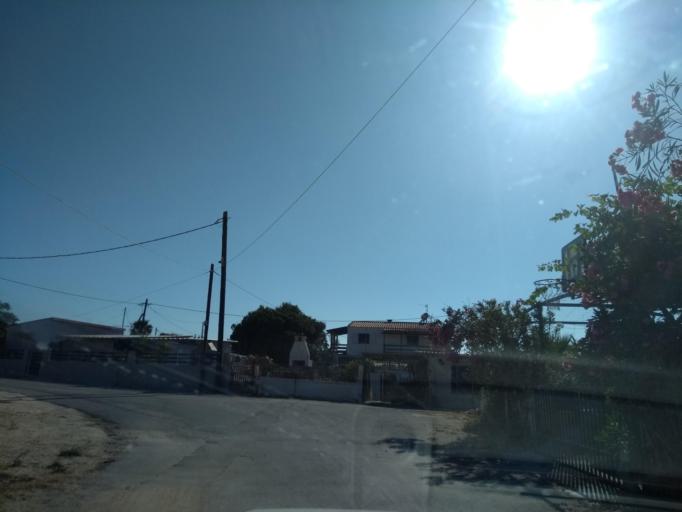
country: GR
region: Crete
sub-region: Nomos Chanias
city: Pithari
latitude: 35.5913
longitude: 24.0928
